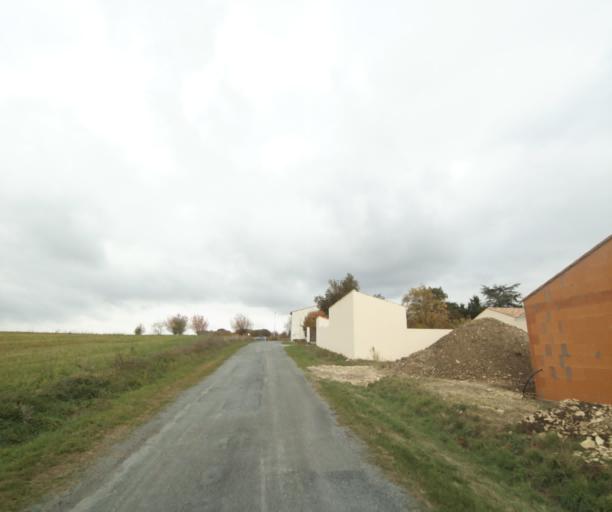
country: FR
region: Poitou-Charentes
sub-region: Departement de la Charente-Maritime
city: Saint-Georges-des-Coteaux
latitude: 45.7692
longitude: -0.7118
